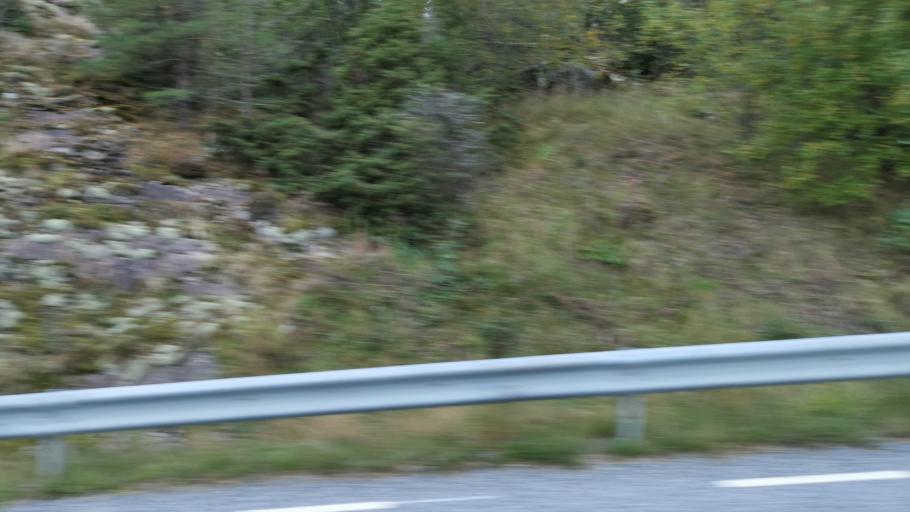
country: SE
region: Vaestra Goetaland
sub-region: Tanums Kommun
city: Tanumshede
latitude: 58.6691
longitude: 11.3423
